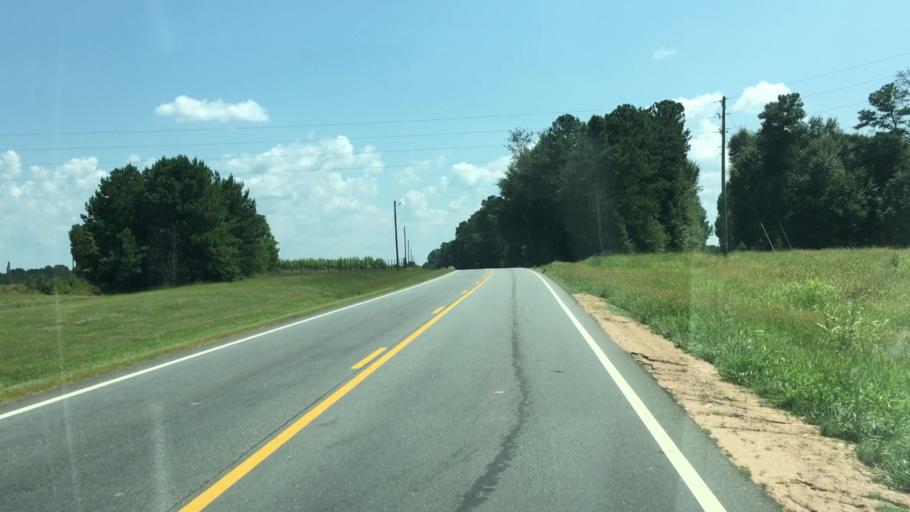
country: US
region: Georgia
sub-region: Oconee County
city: Watkinsville
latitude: 33.7513
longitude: -83.4347
